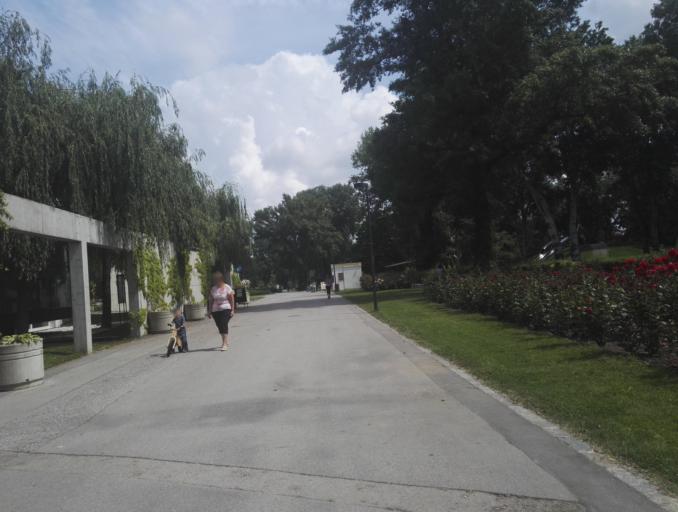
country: AT
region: Vienna
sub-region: Wien Stadt
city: Vienna
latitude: 48.2382
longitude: 16.4170
